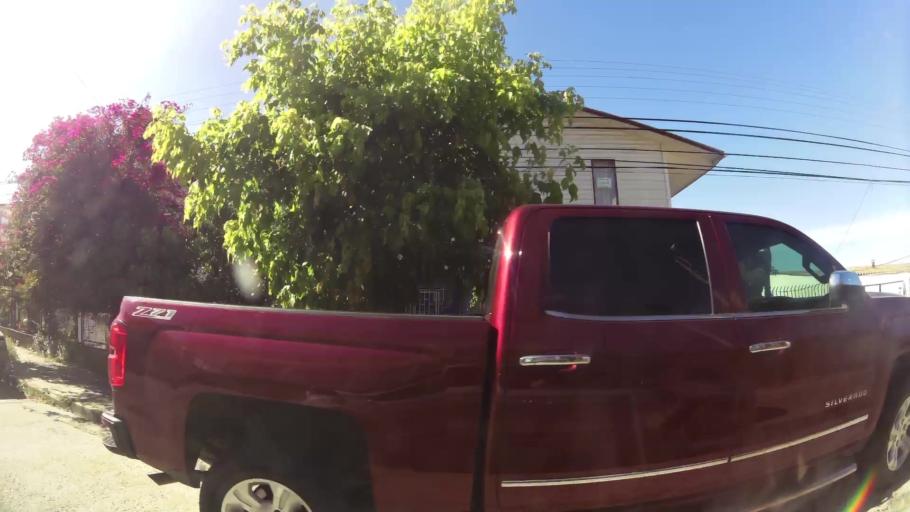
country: CL
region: Valparaiso
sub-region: Provincia de Valparaiso
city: Vina del Mar
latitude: -33.0340
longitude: -71.5630
